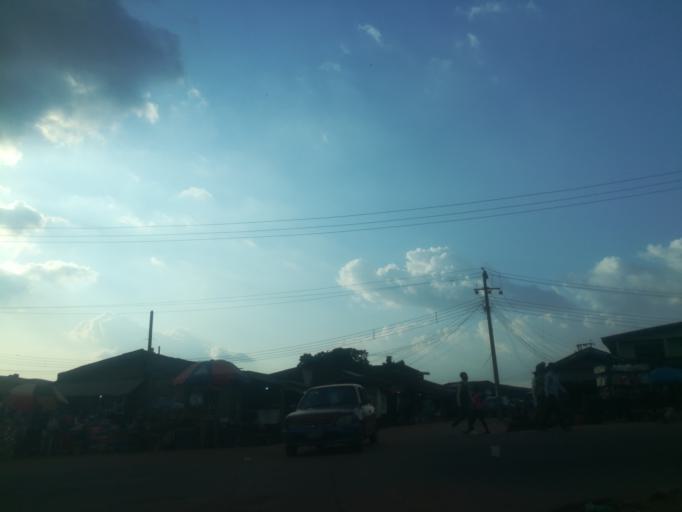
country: NG
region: Oyo
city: Ibadan
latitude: 7.4074
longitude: 3.9462
